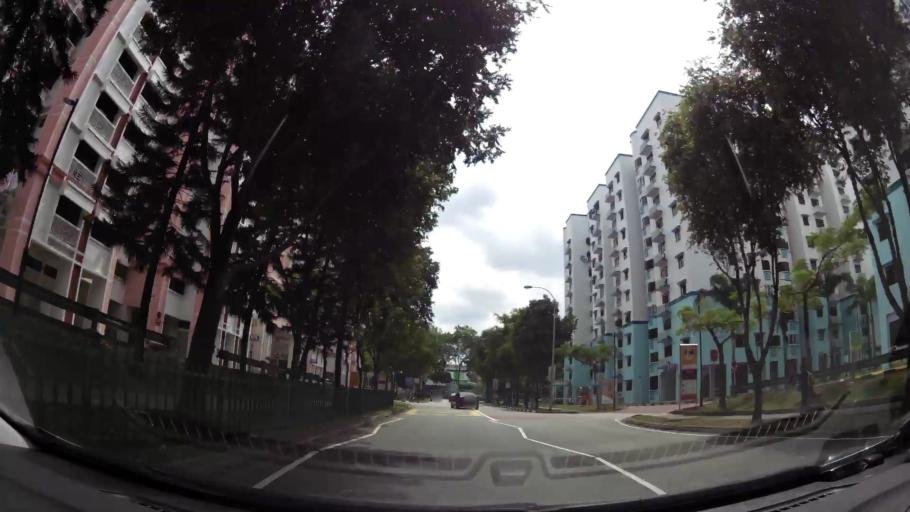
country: MY
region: Johor
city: Johor Bahru
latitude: 1.4022
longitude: 103.7459
